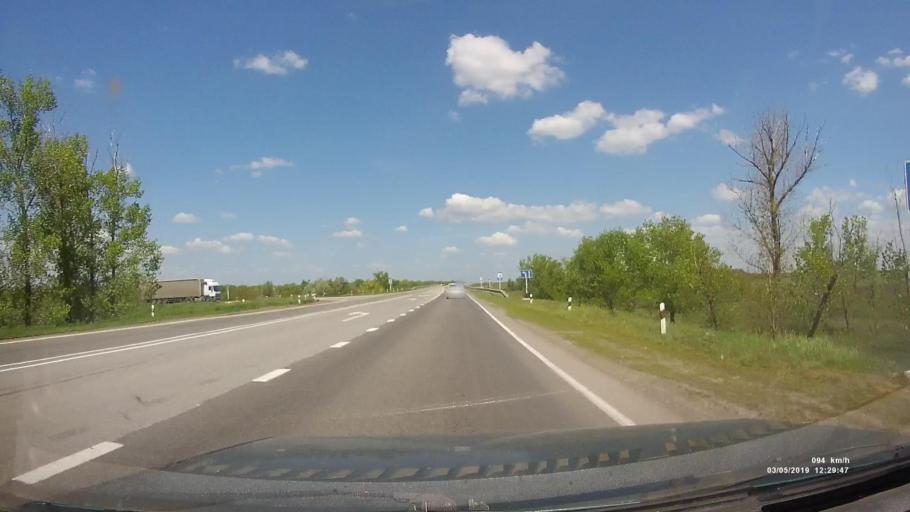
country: RU
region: Rostov
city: Semikarakorsk
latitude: 47.4926
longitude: 40.7383
